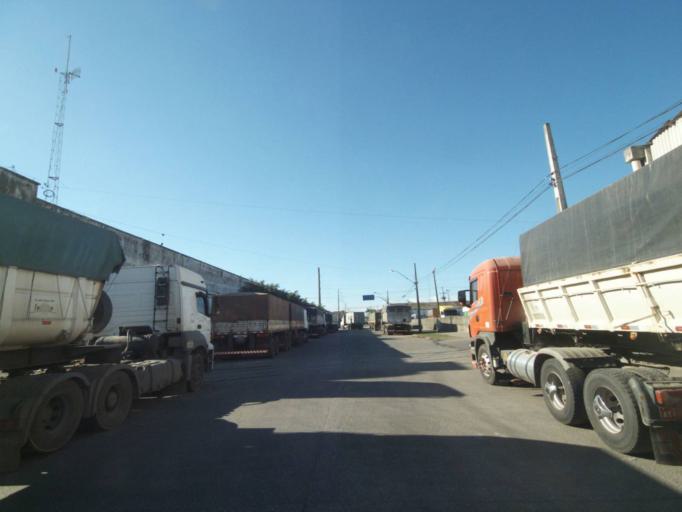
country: BR
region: Parana
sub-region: Paranagua
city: Paranagua
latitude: -25.5107
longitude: -48.5121
